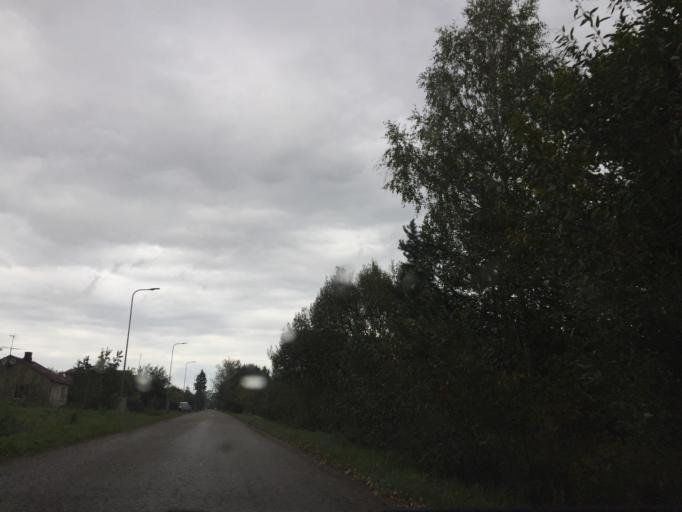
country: LV
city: Tireli
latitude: 56.7812
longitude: 23.6333
